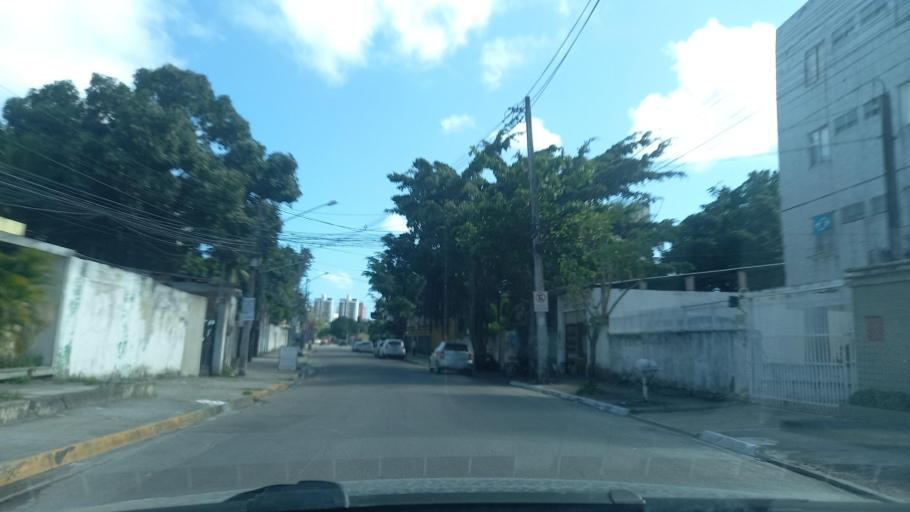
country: BR
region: Pernambuco
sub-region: Jaboatao Dos Guararapes
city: Jaboatao
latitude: -8.1956
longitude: -34.9220
